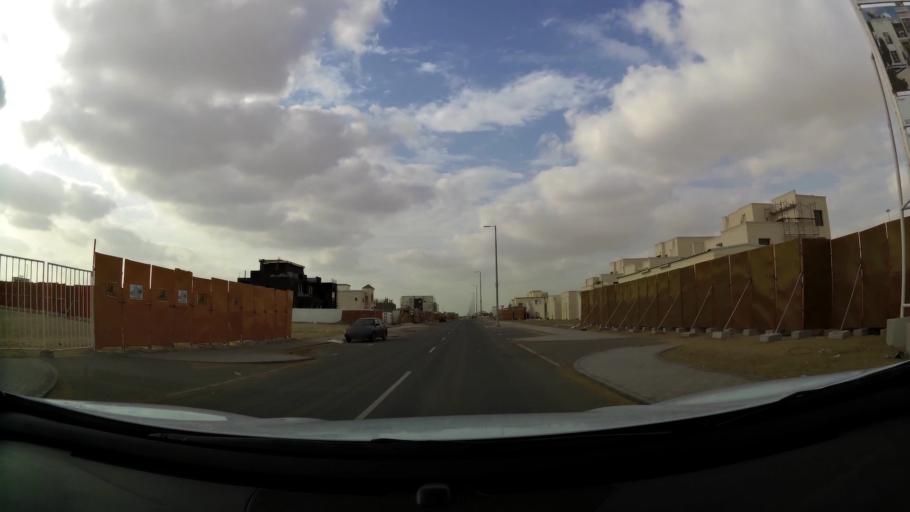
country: AE
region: Abu Dhabi
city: Abu Dhabi
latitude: 24.3341
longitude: 54.5792
